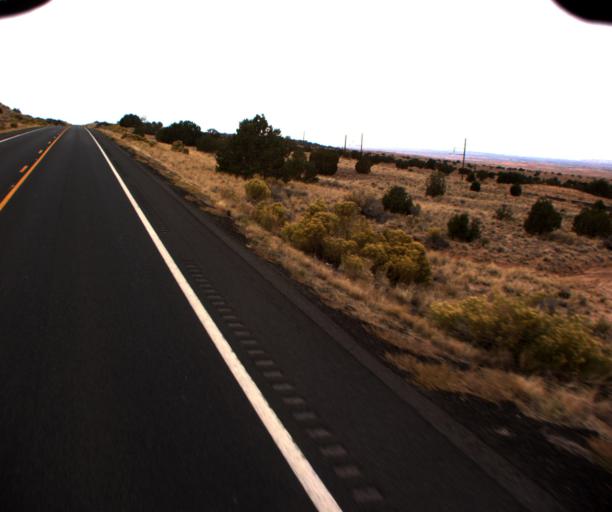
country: US
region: Arizona
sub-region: Coconino County
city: Kaibito
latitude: 36.4521
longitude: -110.7138
